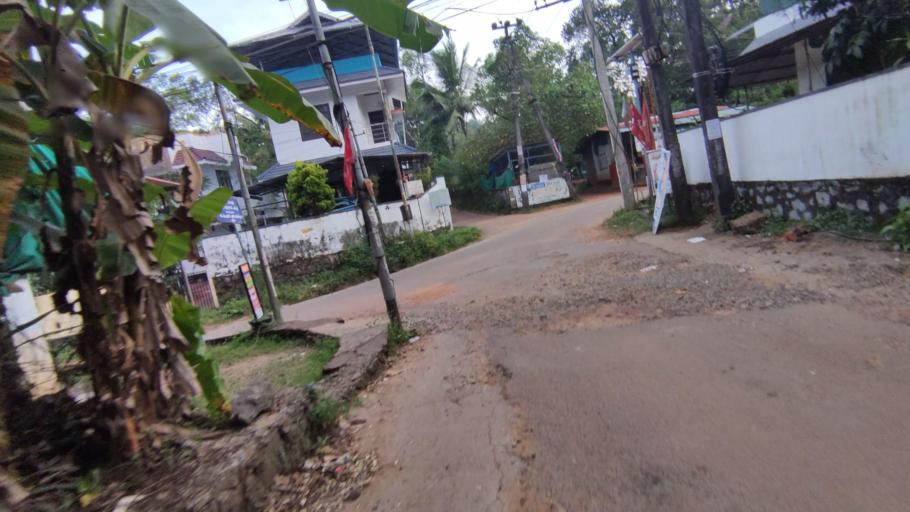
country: IN
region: Kerala
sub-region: Kottayam
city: Kottayam
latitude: 9.6347
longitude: 76.5045
